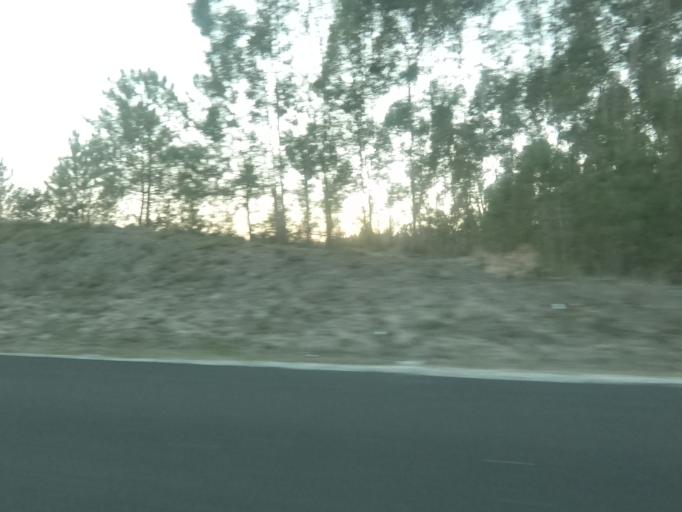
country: PT
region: Leiria
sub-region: Pombal
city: Pombal
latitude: 39.8727
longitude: -8.7029
